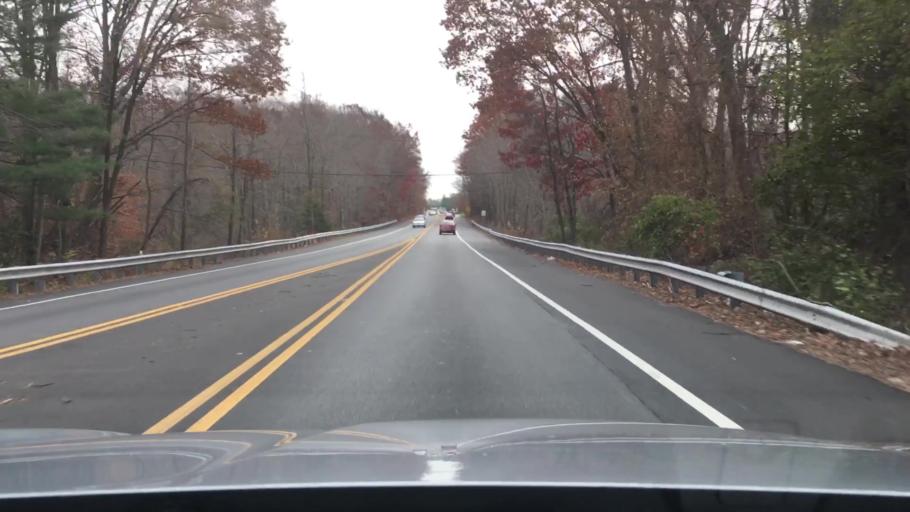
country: US
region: Maryland
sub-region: Prince George's County
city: Bowie
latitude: 38.9619
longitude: -76.7511
